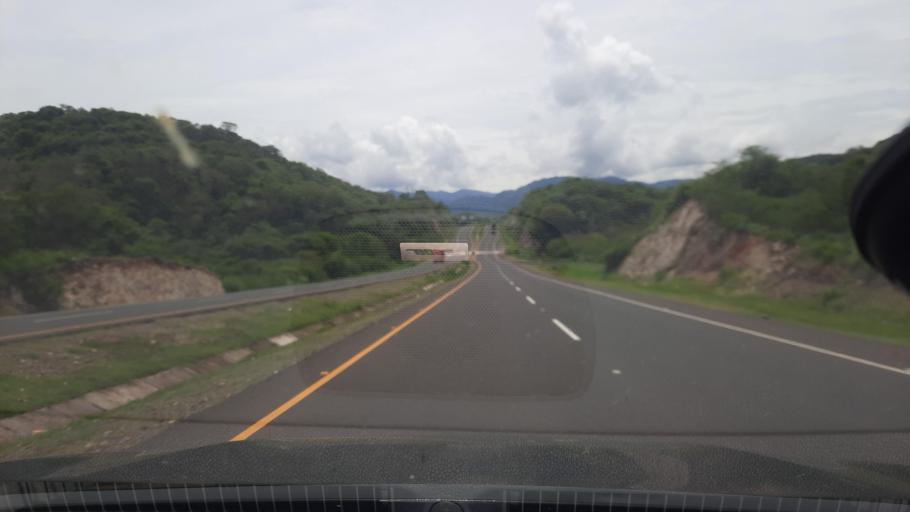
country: HN
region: Valle
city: Aramecina
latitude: 13.6890
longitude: -87.7206
